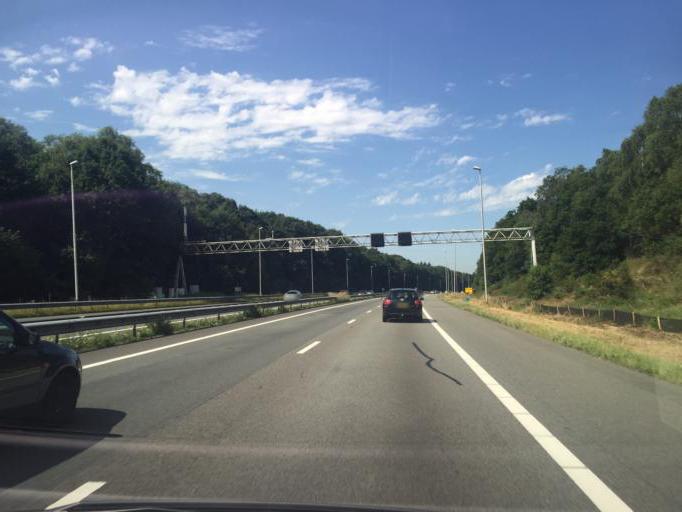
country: NL
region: Gelderland
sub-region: Gemeente Ede
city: Bennekom
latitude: 52.0136
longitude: 5.6975
